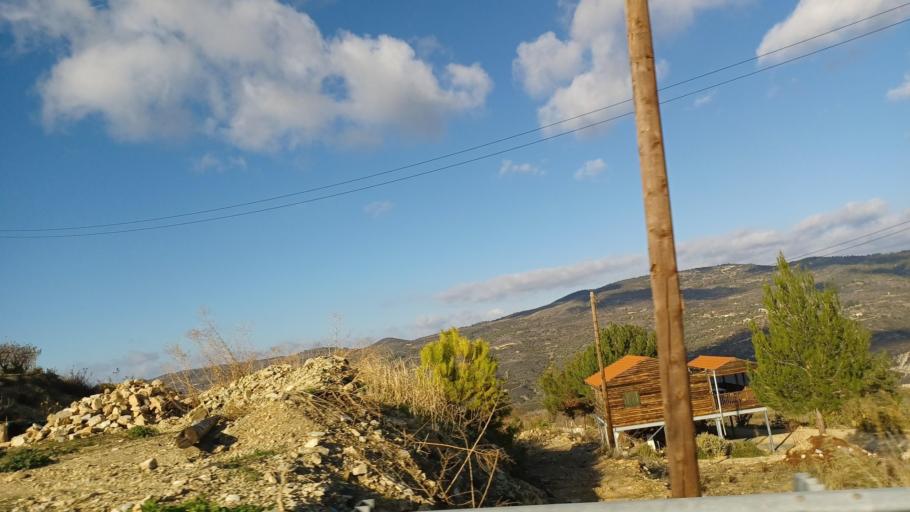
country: CY
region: Limassol
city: Pachna
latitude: 34.8480
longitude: 32.7395
